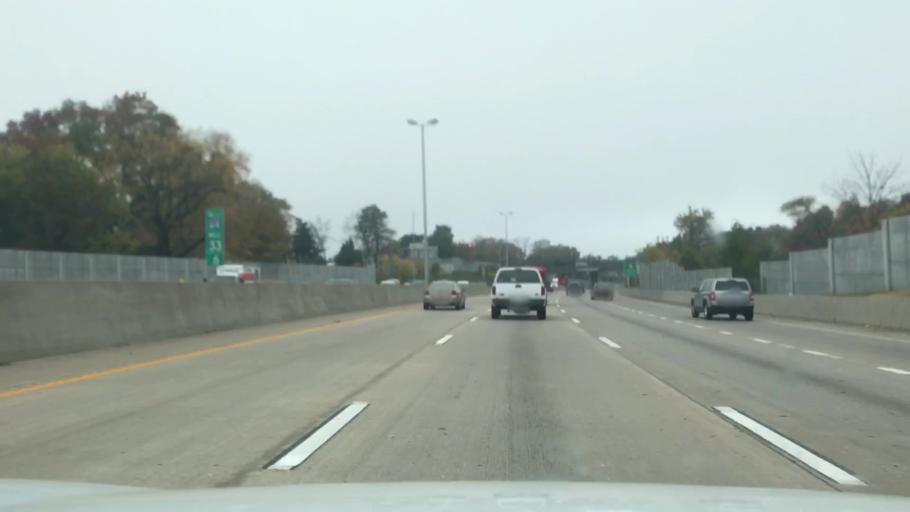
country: US
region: Missouri
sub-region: Saint Louis County
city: Richmond Heights
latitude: 38.6291
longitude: -90.3091
